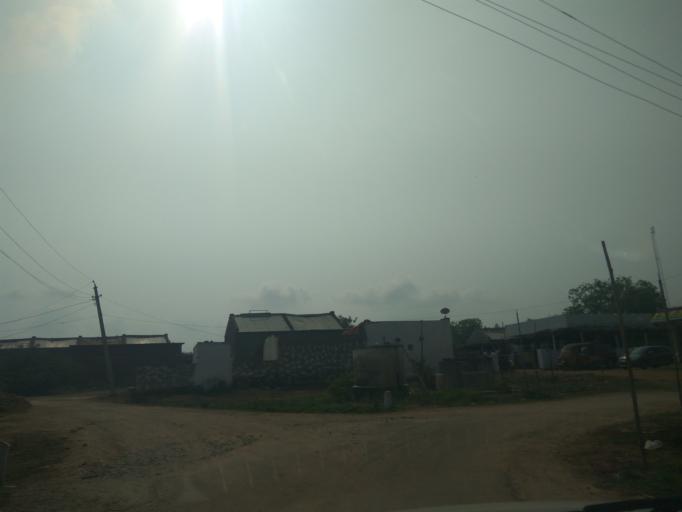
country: IN
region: Andhra Pradesh
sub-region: Prakasam
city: Kandukur
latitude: 15.0746
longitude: 79.6095
